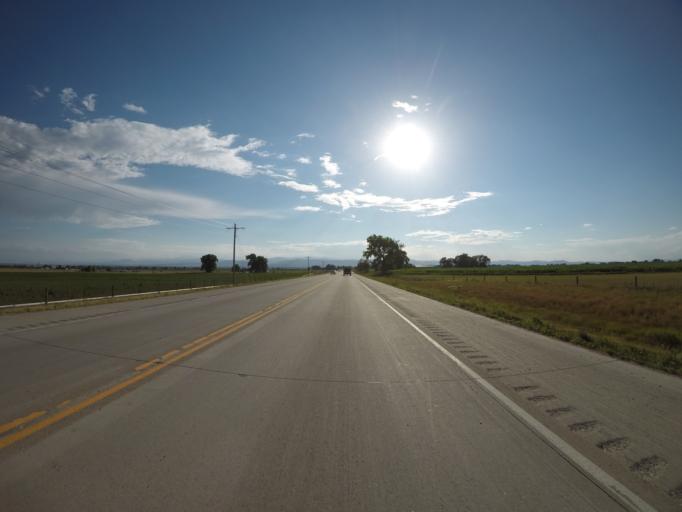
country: US
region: Colorado
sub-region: Weld County
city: Severance
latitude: 40.5812
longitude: -104.9359
